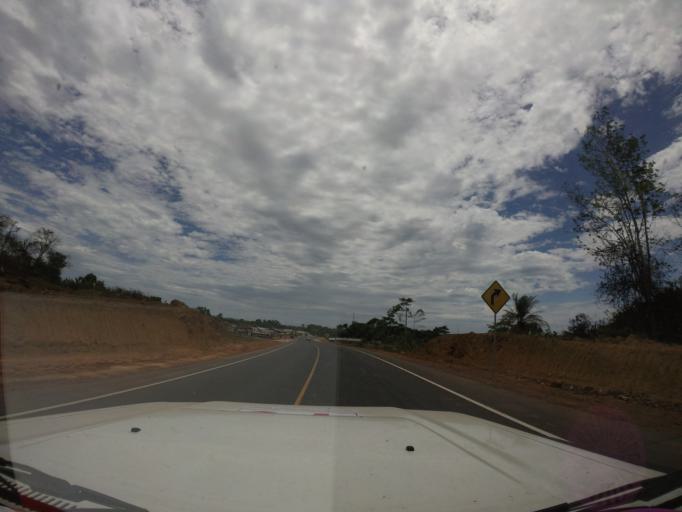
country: LR
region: Margibi
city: Kakata
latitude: 6.6857
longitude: -10.2108
